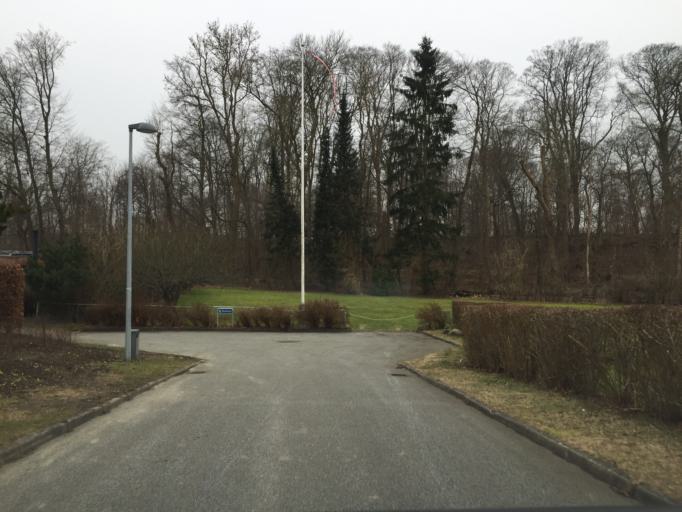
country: DK
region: Capital Region
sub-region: Fureso Kommune
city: Farum
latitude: 55.8079
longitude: 12.3637
